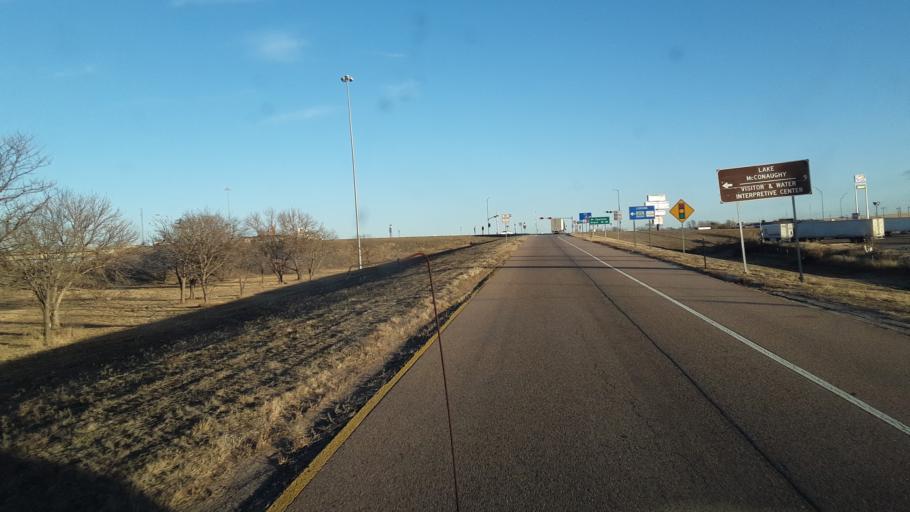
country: US
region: Nebraska
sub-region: Keith County
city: Ogallala
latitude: 41.1146
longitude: -101.7179
